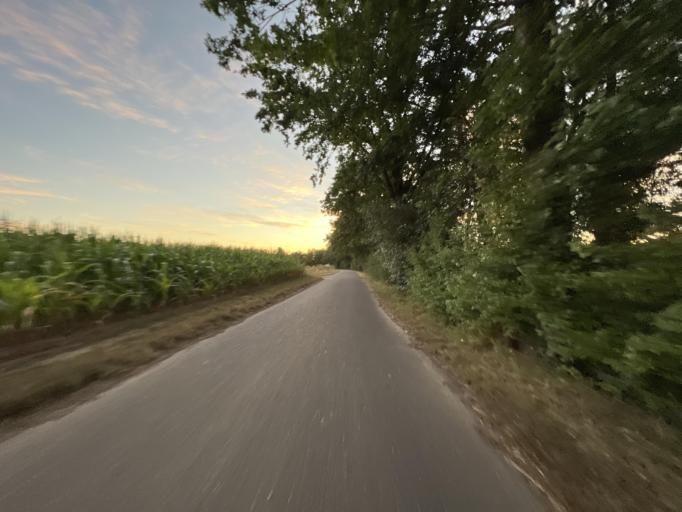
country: DE
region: North Rhine-Westphalia
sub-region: Regierungsbezirk Koln
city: Dueren
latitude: 50.7802
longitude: 6.4581
